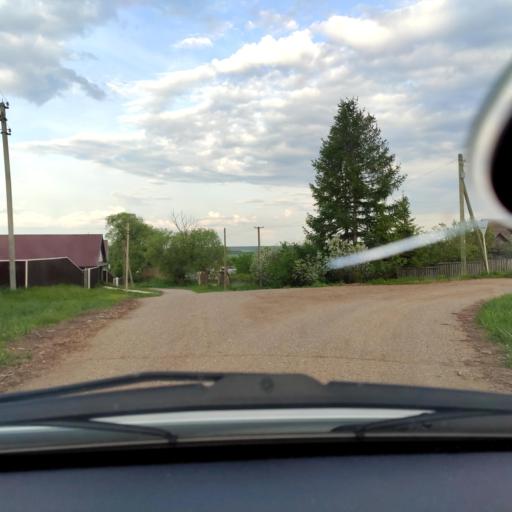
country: RU
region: Bashkortostan
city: Dyurtyuli
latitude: 55.5913
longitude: 54.9547
